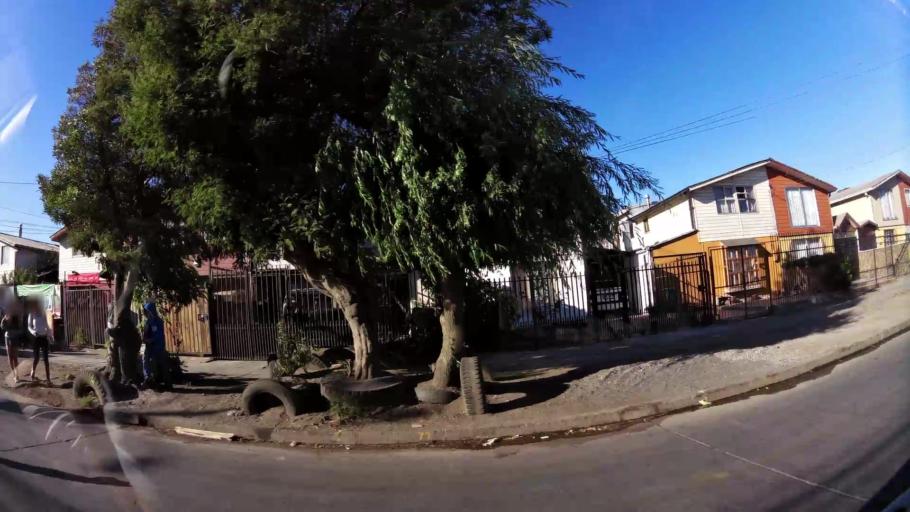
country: CL
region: Biobio
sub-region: Provincia de Concepcion
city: Concepcion
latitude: -36.8288
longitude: -73.1242
